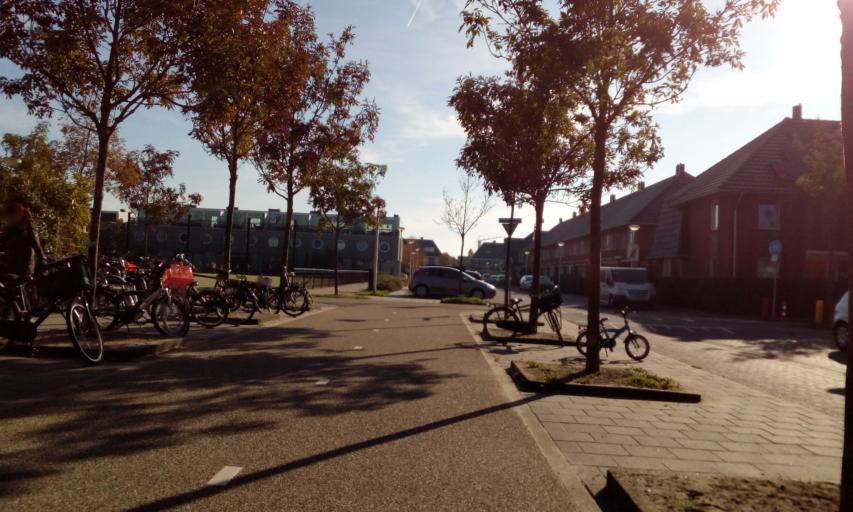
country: NL
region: Utrecht
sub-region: Stichtse Vecht
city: Spechtenkamp
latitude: 52.0954
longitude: 5.0023
